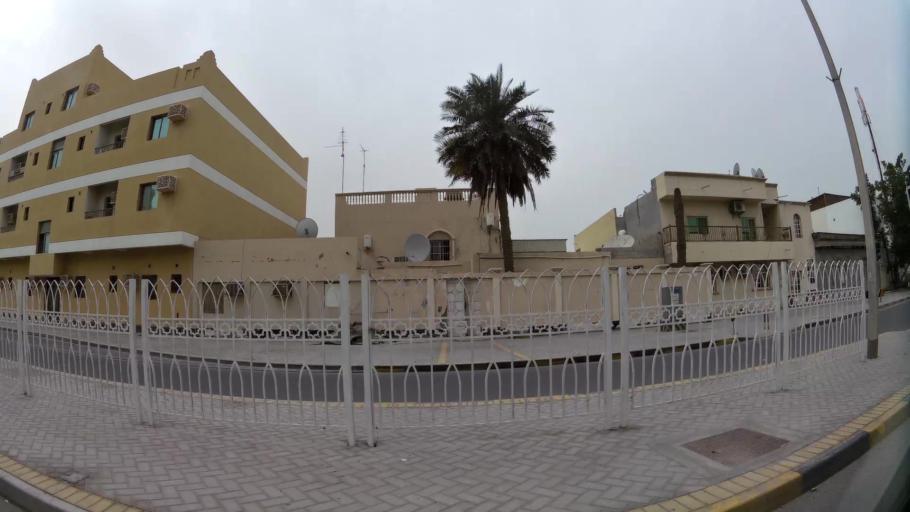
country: BH
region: Northern
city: Madinat `Isa
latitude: 26.1723
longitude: 50.5458
